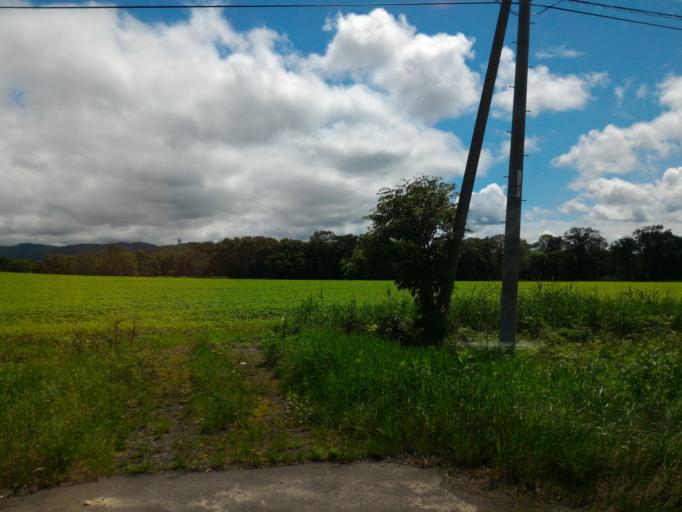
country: JP
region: Hokkaido
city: Nayoro
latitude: 44.6530
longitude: 142.2676
